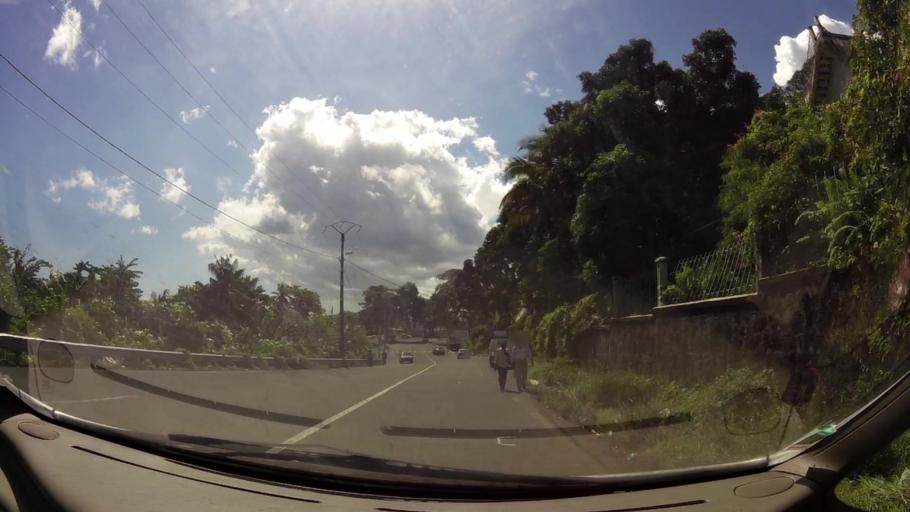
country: KM
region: Grande Comore
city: Mavingouni
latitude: -11.7115
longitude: 43.2462
